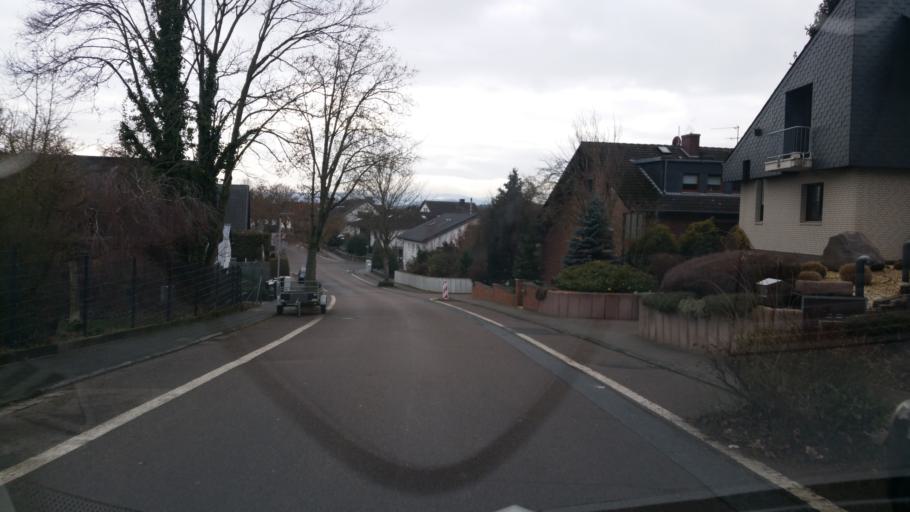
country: DE
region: Hesse
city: Reinheim
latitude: 49.8305
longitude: 8.8232
